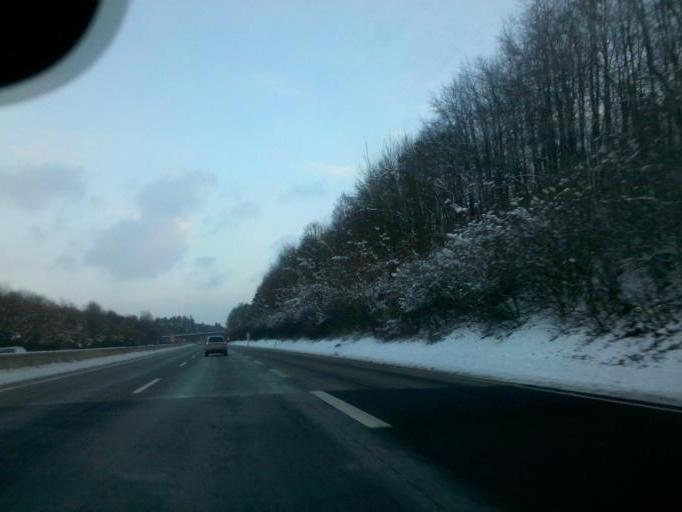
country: DE
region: North Rhine-Westphalia
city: Freudenberg
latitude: 50.9327
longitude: 7.8845
